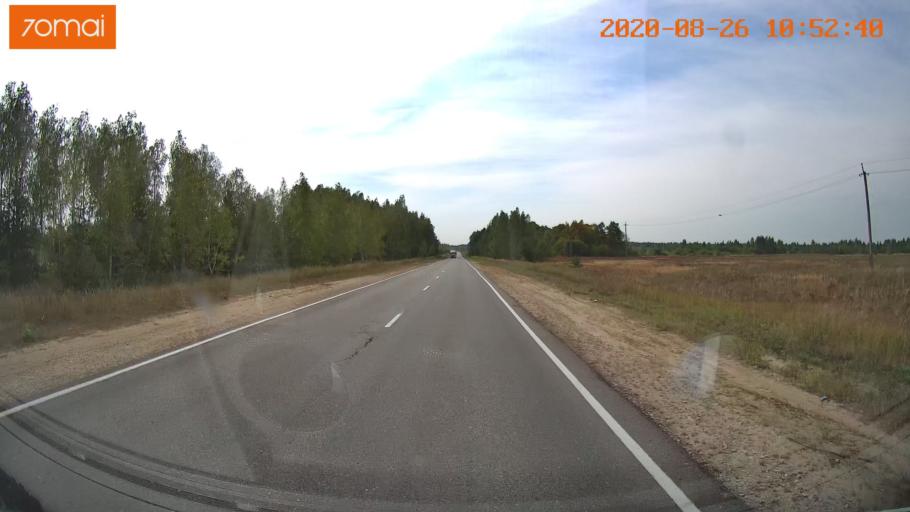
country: RU
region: Rjazan
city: Lashma
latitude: 54.6532
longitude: 41.1538
